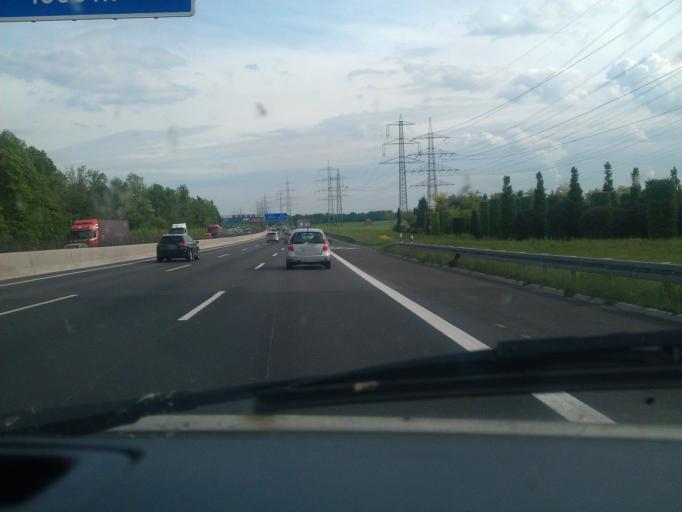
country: DE
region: North Rhine-Westphalia
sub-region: Regierungsbezirk Dusseldorf
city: Neuss
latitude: 51.1955
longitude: 6.6555
